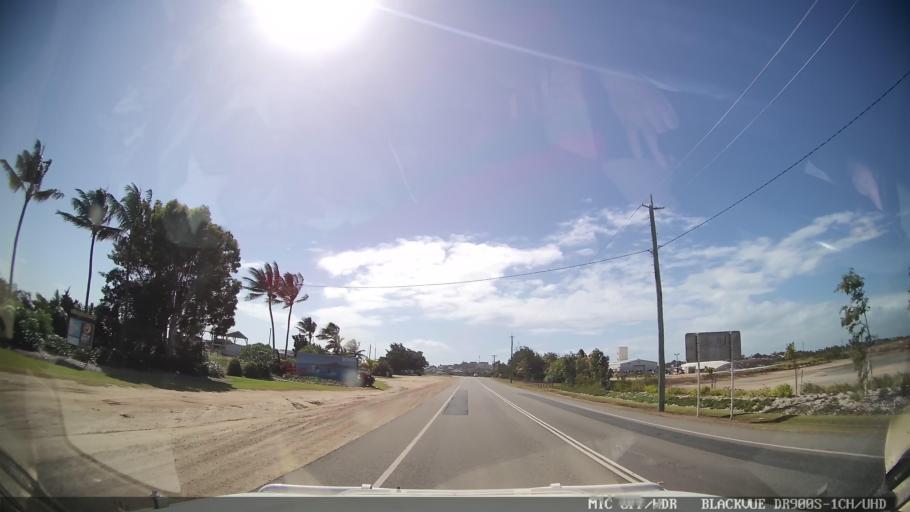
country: AU
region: Queensland
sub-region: Whitsunday
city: Bowen
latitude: -20.0138
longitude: 148.2233
